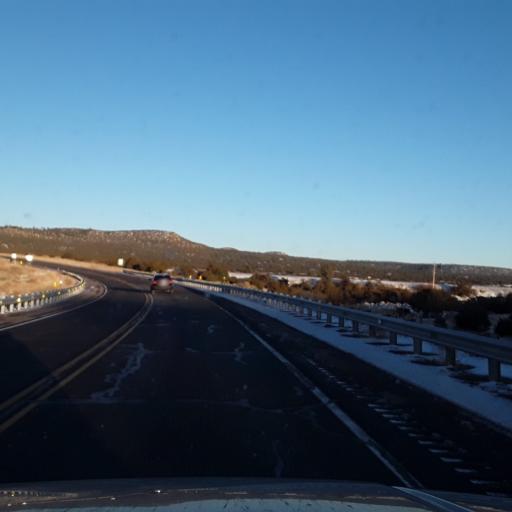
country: US
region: New Mexico
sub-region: Lincoln County
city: Carrizozo
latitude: 34.2395
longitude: -105.6003
